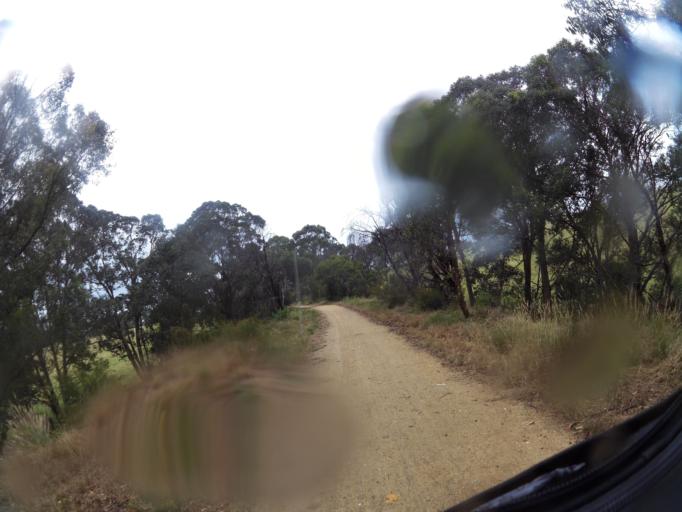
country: AU
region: Victoria
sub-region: East Gippsland
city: Lakes Entrance
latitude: -37.7613
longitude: 147.8175
